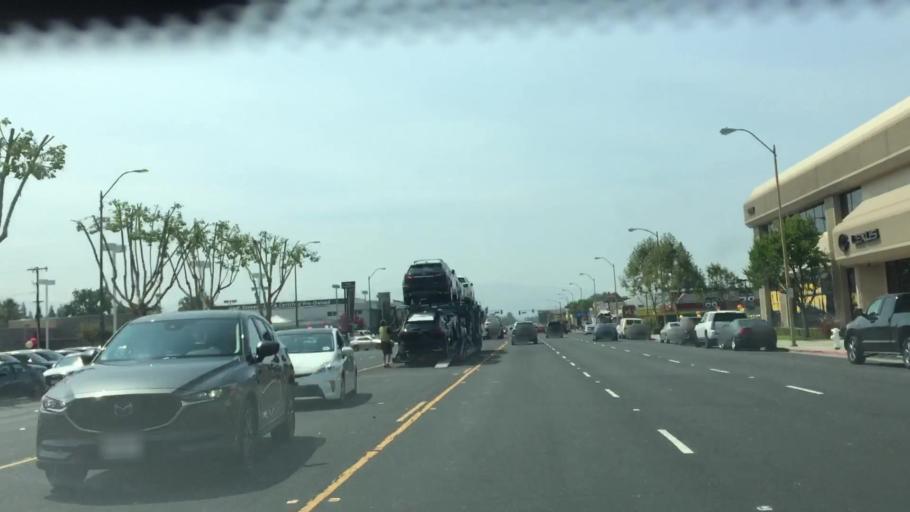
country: US
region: California
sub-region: Santa Clara County
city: Burbank
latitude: 37.3229
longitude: -121.9568
